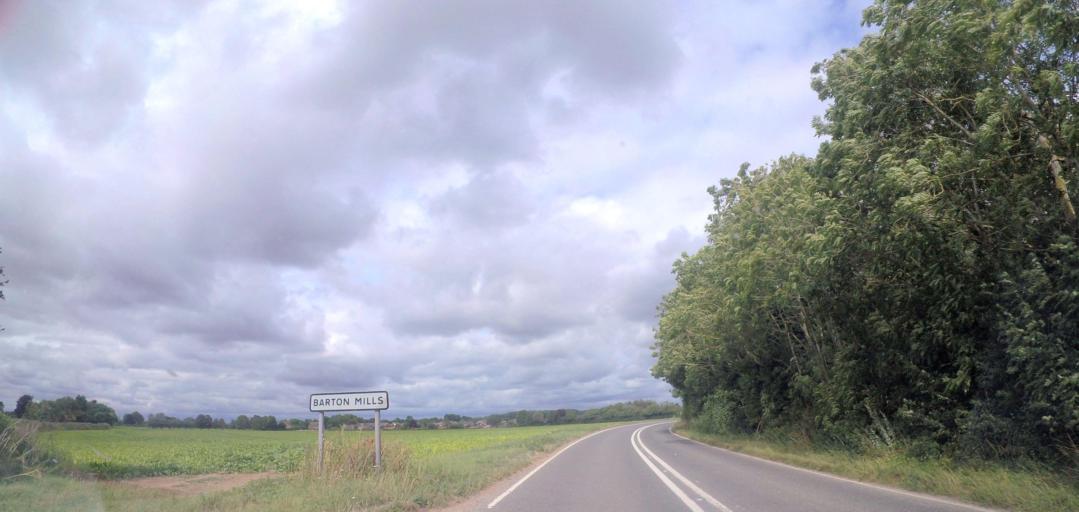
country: GB
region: England
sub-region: Suffolk
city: Lakenheath
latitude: 52.3292
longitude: 0.5139
